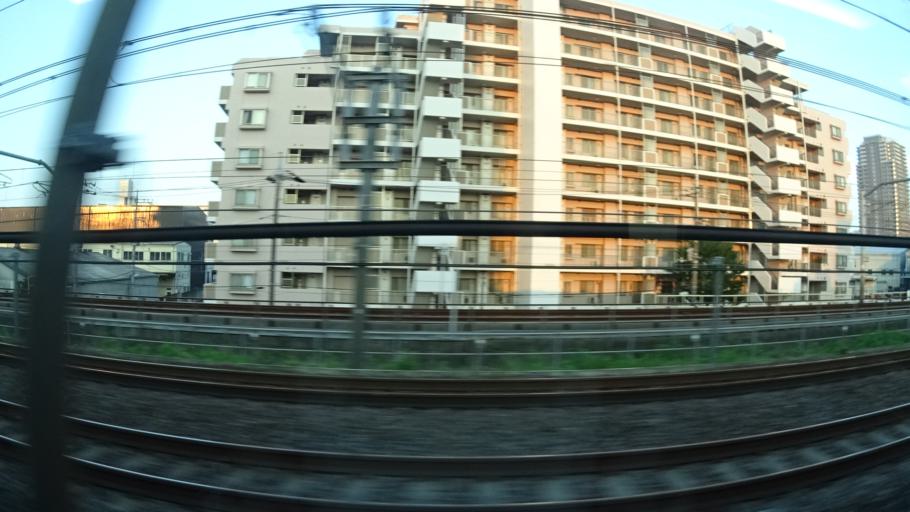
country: JP
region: Saitama
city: Soka
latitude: 35.7407
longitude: 139.8019
